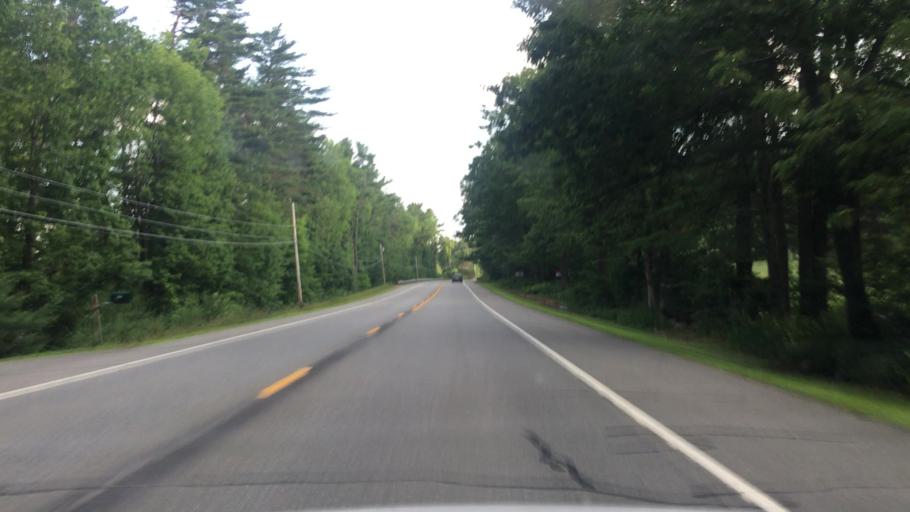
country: US
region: Maine
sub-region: Kennebec County
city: Windsor
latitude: 44.3547
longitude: -69.6447
